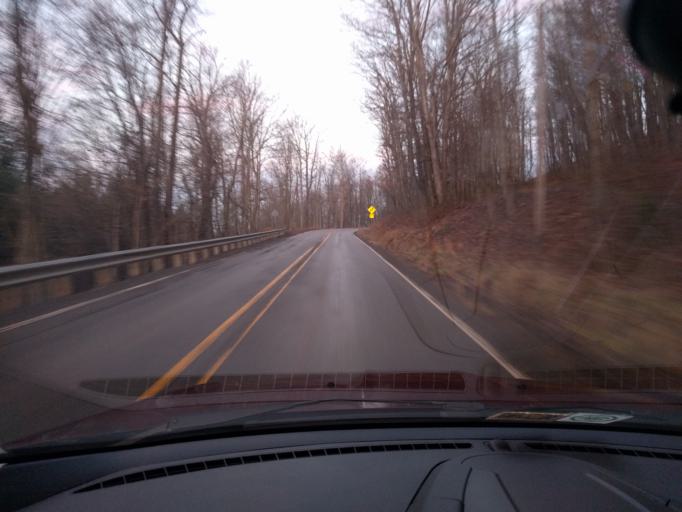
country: US
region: West Virginia
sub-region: Greenbrier County
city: Rainelle
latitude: 37.9969
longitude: -80.8704
